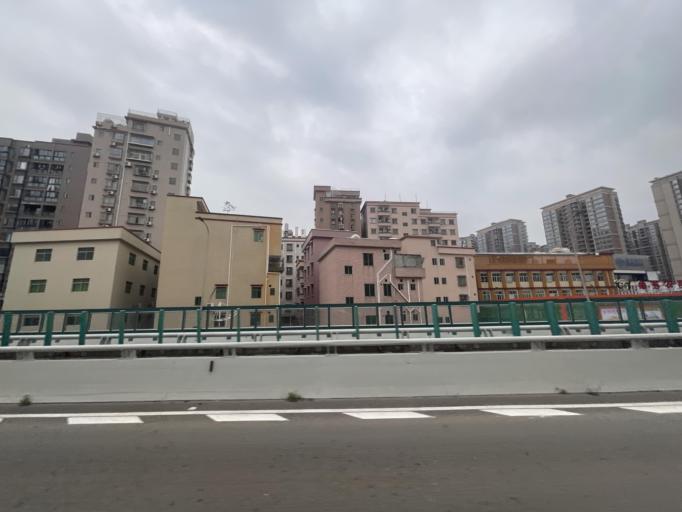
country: CN
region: Guangdong
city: Humen
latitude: 22.8061
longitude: 113.6817
